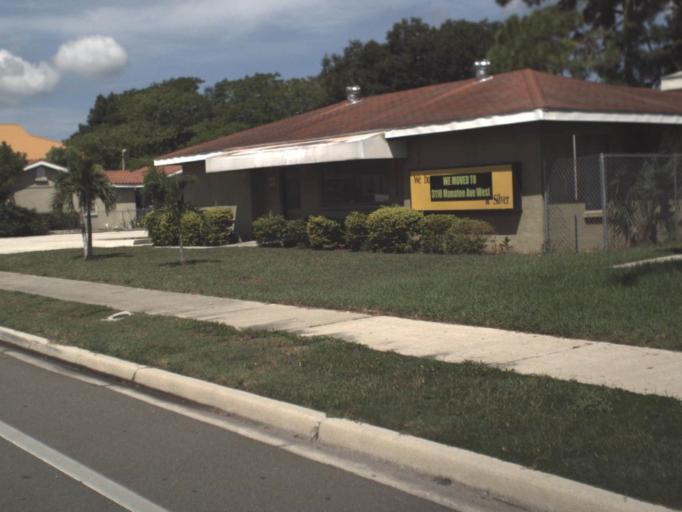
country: US
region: Florida
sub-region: Manatee County
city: West Bradenton
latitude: 27.4959
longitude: -82.6094
